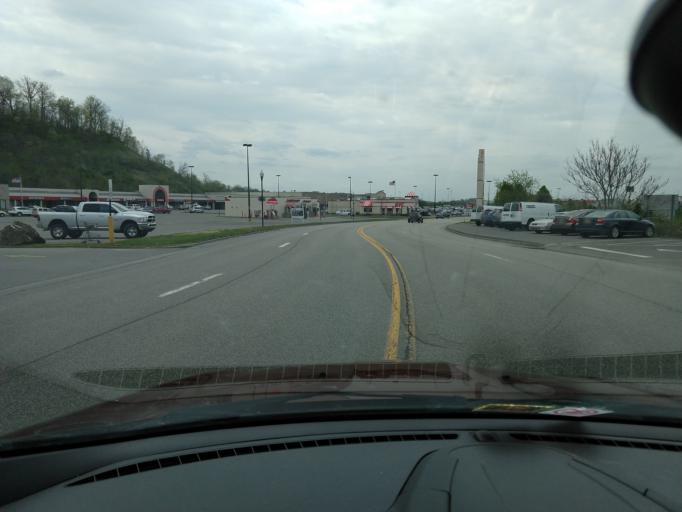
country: US
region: West Virginia
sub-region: Harrison County
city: Bridgeport
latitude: 39.2790
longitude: -80.2813
